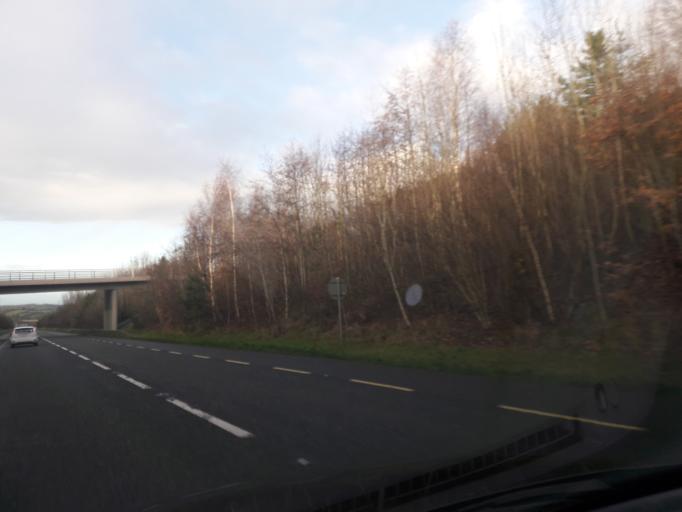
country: IE
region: Ulster
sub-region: County Monaghan
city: Carrickmacross
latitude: 53.9783
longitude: -6.7054
